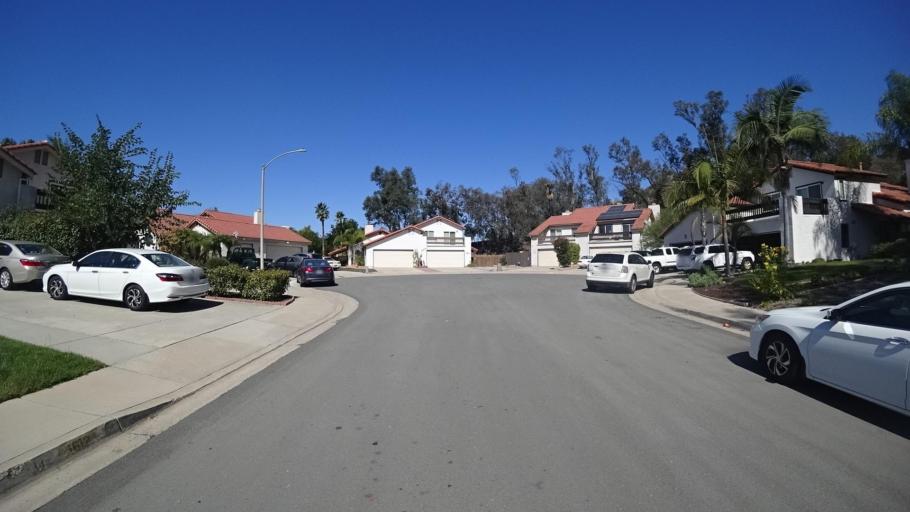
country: US
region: California
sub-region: San Diego County
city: Rancho San Diego
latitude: 32.7501
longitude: -116.9236
